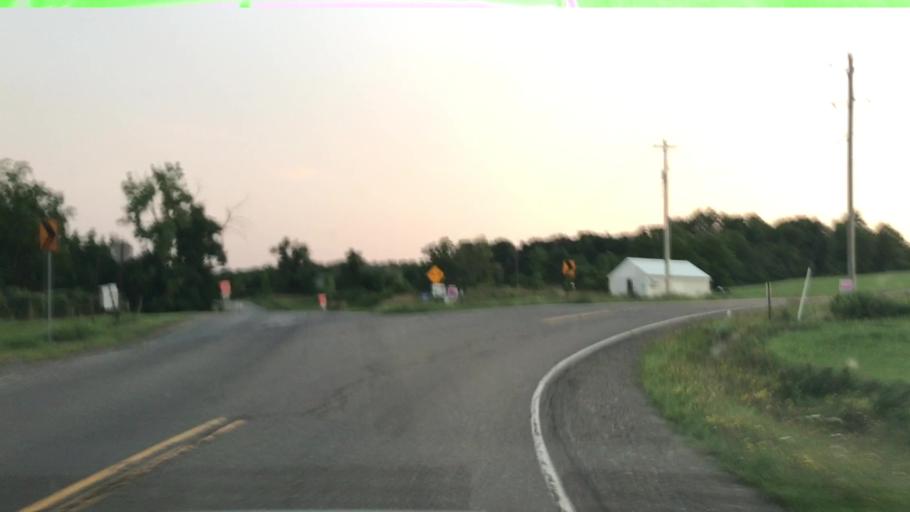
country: US
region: New York
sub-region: Steuben County
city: Sylvan Beach
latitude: 42.5132
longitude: -77.1788
